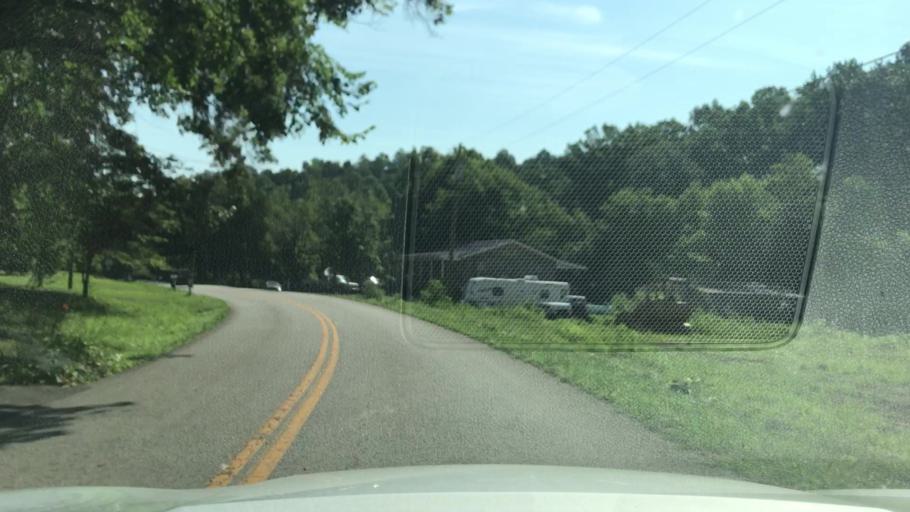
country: US
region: Kentucky
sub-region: Clinton County
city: Albany
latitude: 36.7428
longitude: -84.9976
